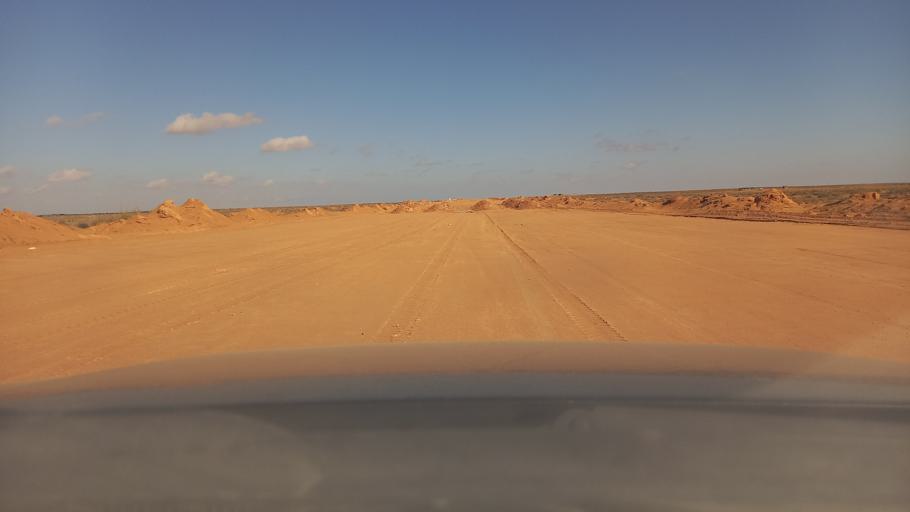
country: TN
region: Madanin
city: Medenine
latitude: 33.2387
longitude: 10.5539
